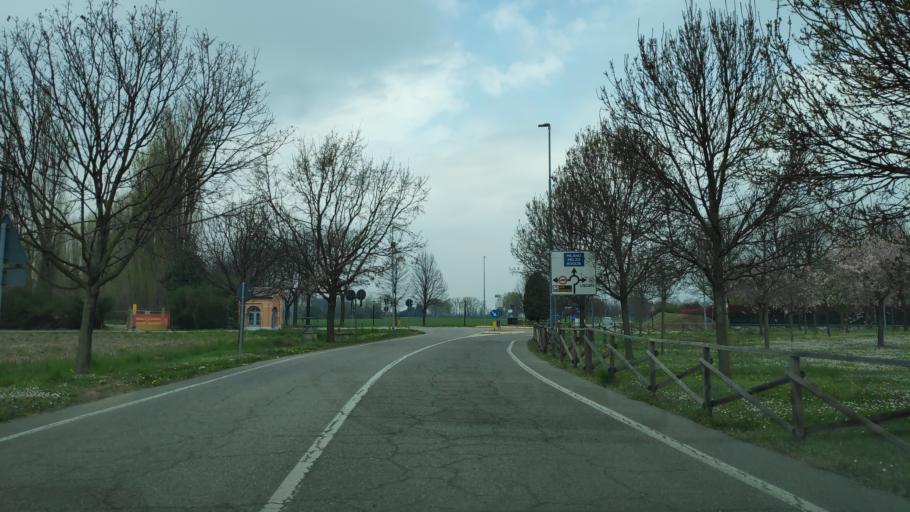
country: IT
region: Lombardy
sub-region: Citta metropolitana di Milano
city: Liscate
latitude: 45.4795
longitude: 9.4037
